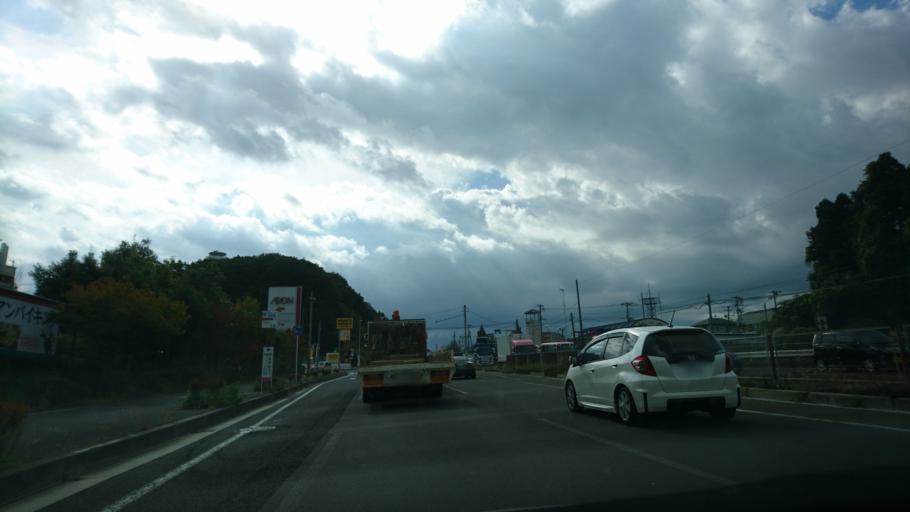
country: JP
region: Miyagi
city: Tomiya
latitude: 38.3635
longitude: 140.8731
